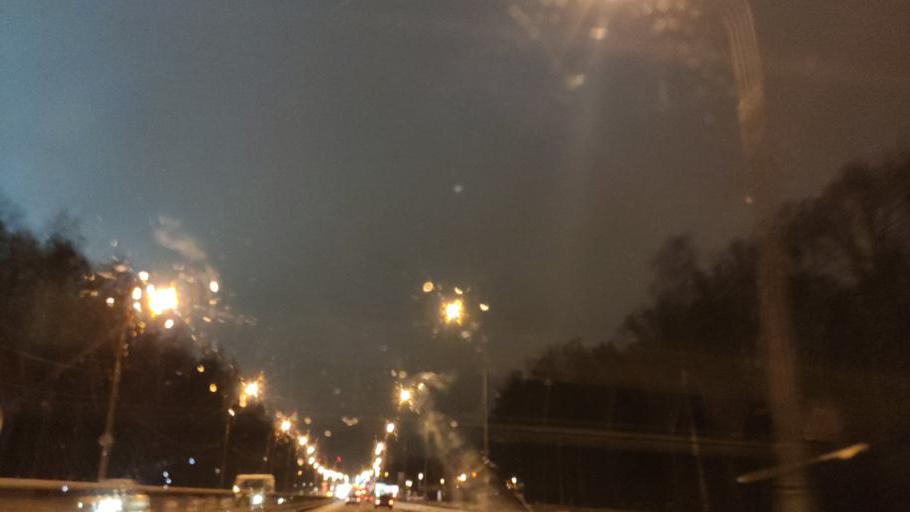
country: RU
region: Moskovskaya
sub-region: Leninskiy Rayon
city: Vnukovo
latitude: 55.6030
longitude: 37.3018
